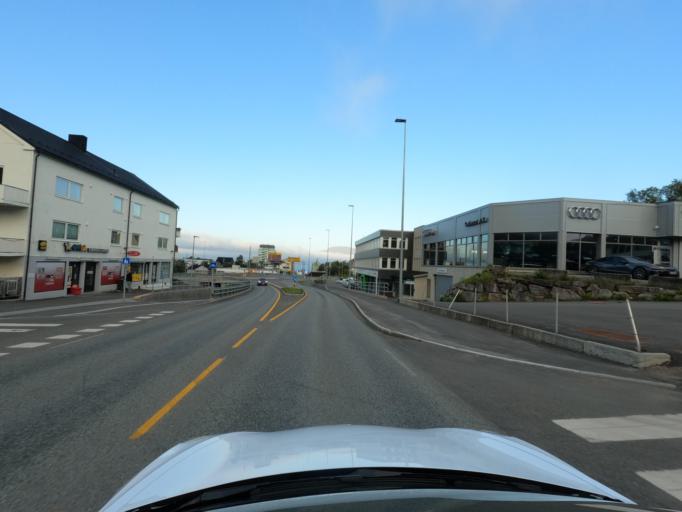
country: NO
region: Troms
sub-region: Harstad
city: Harstad
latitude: 68.8059
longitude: 16.5294
